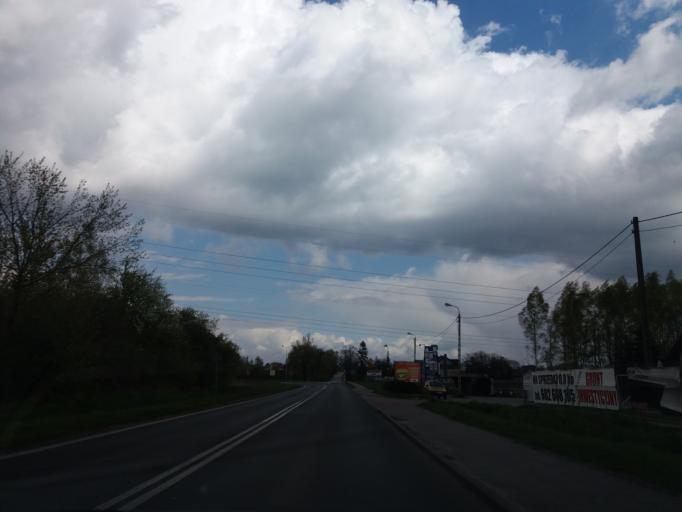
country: PL
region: Silesian Voivodeship
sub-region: Powiat bierunsko-ledzinski
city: Chelm Slaski
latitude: 50.0871
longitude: 19.2008
